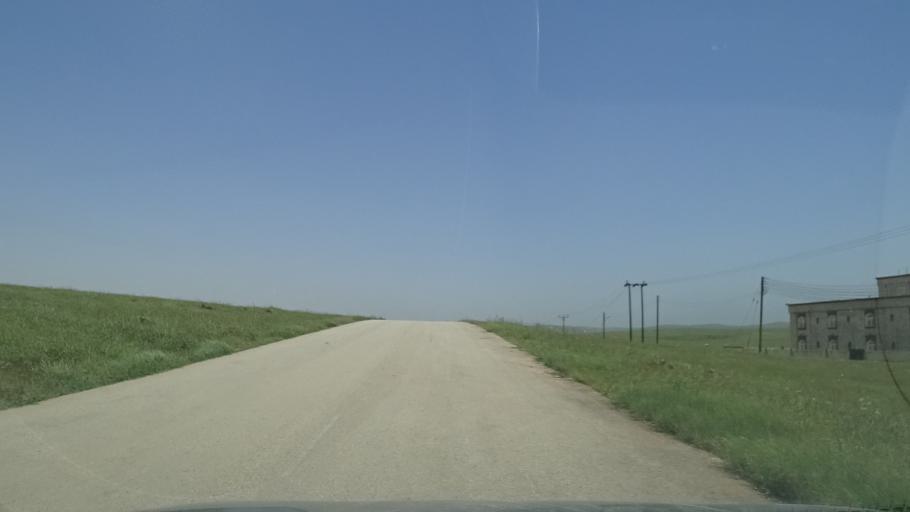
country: OM
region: Zufar
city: Salalah
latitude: 17.2493
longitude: 54.2709
